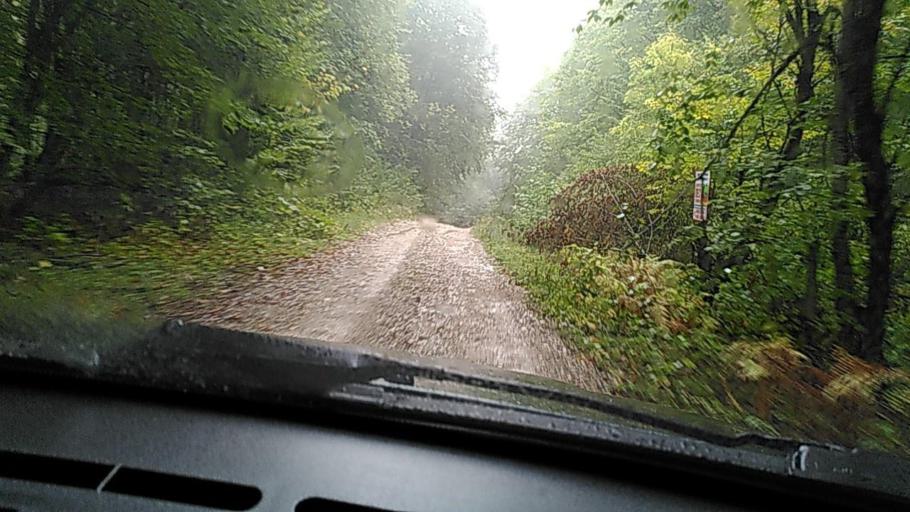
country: RU
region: Kabardino-Balkariya
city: Belaya Rechka
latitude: 43.3735
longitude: 43.4283
